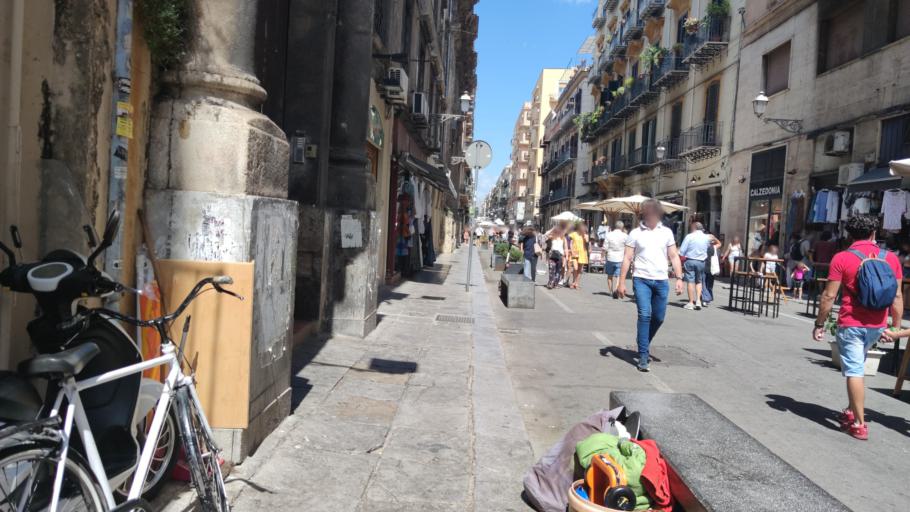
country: IT
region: Sicily
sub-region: Palermo
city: Palermo
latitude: 38.1164
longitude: 13.3610
